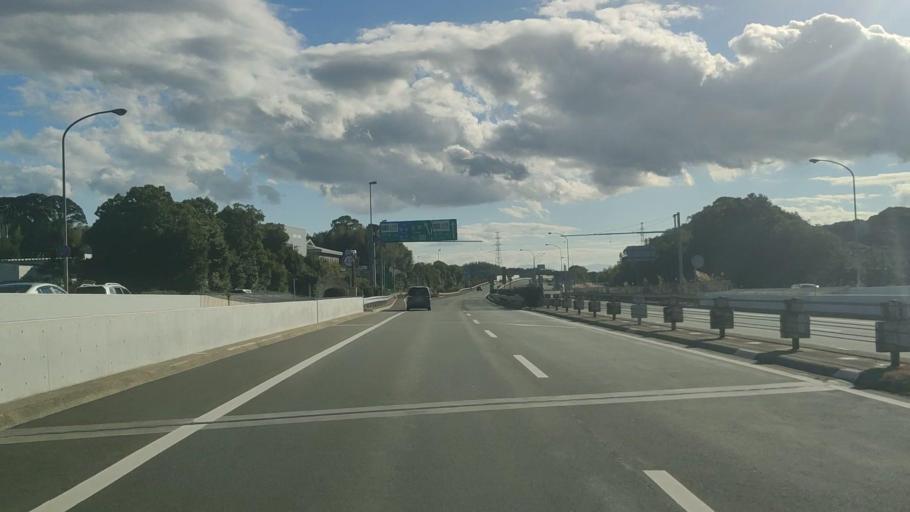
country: JP
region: Fukuoka
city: Nakama
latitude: 33.7888
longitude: 130.7458
